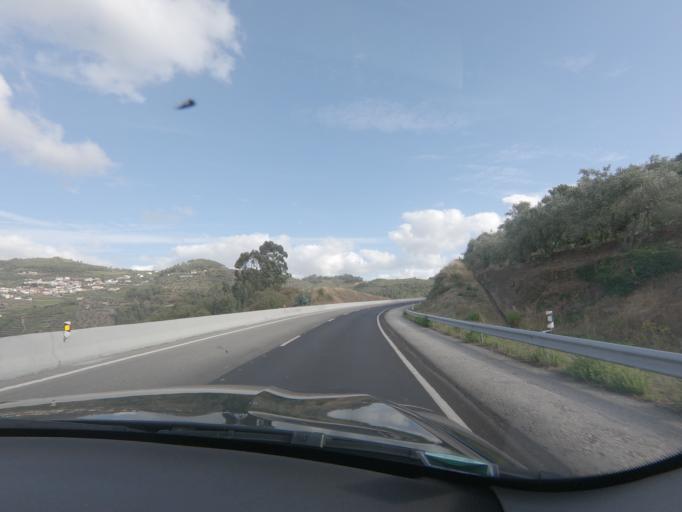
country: PT
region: Viseu
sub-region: Lamego
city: Lamego
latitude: 41.1047
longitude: -7.7752
